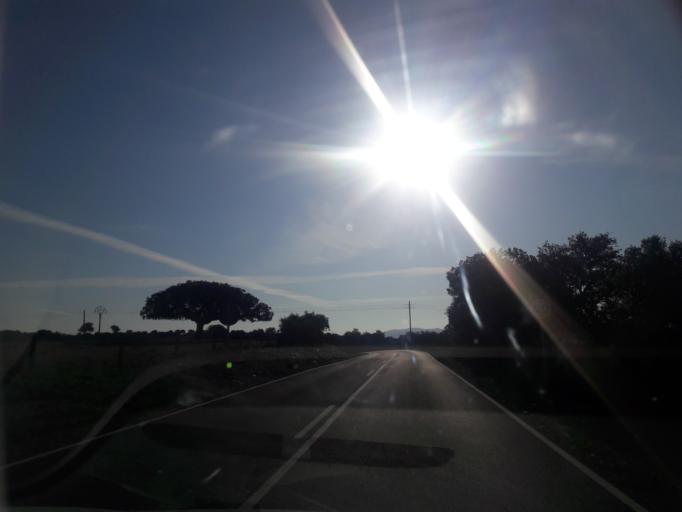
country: ES
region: Castille and Leon
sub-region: Provincia de Salamanca
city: Aldeavieja de Tormes
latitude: 40.5775
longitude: -5.6422
